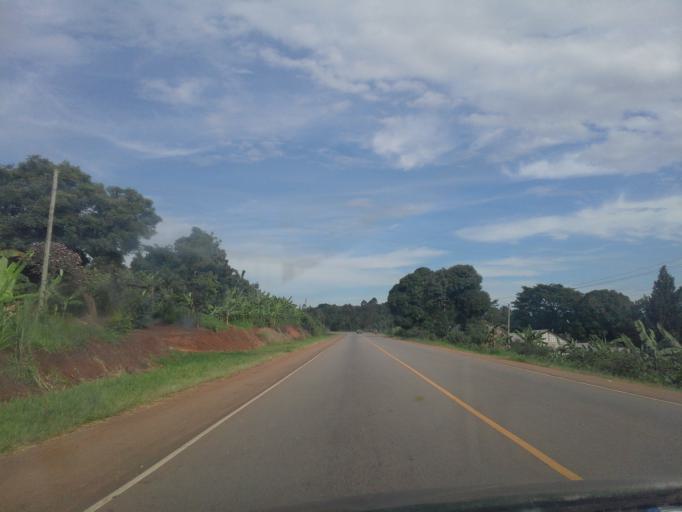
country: UG
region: Central Region
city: Masaka
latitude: -0.3453
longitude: 31.6217
